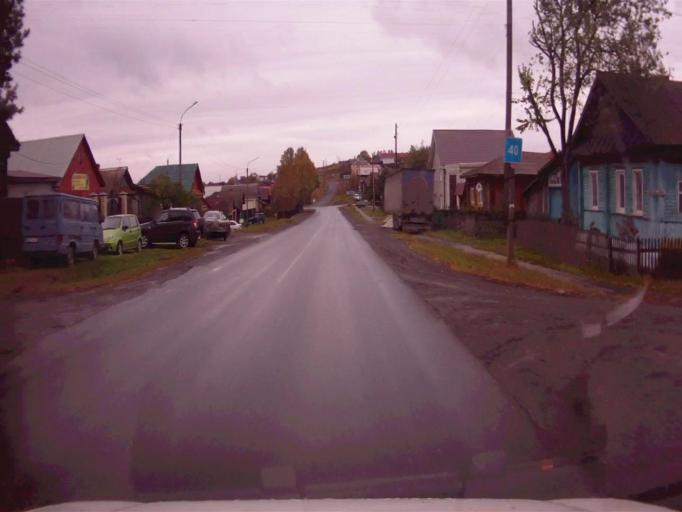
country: RU
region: Chelyabinsk
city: Verkhniy Ufaley
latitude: 56.0570
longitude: 60.2043
